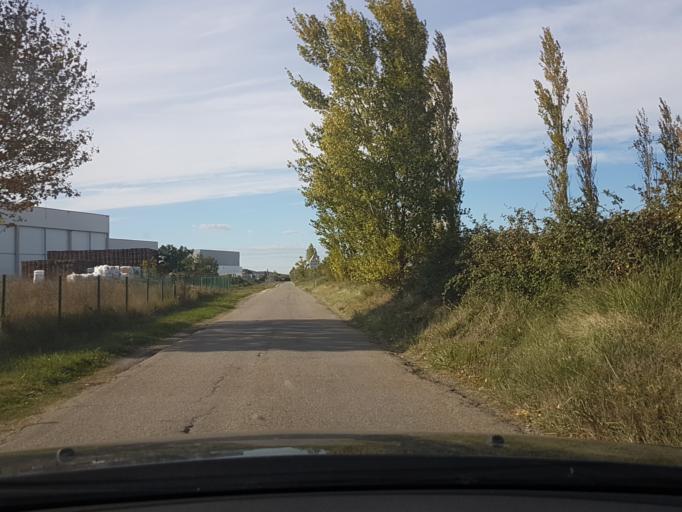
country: FR
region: Provence-Alpes-Cote d'Azur
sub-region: Departement du Vaucluse
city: Entraigues-sur-la-Sorgue
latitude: 43.9836
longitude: 4.9363
